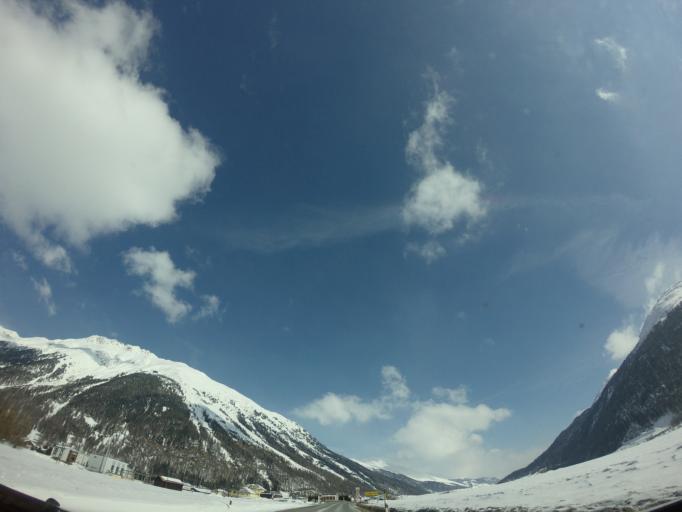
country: CH
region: Grisons
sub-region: Maloja District
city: Samedan
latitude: 46.5462
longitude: 9.8890
